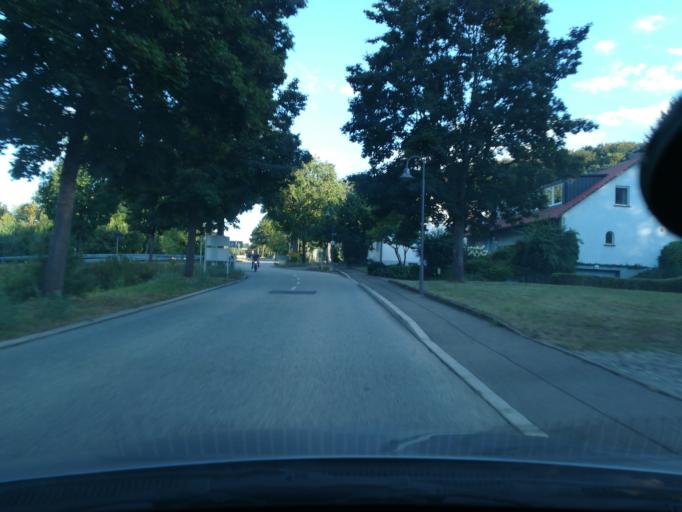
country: DE
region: Baden-Wuerttemberg
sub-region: Freiburg Region
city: Moos
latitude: 47.7344
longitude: 8.8983
